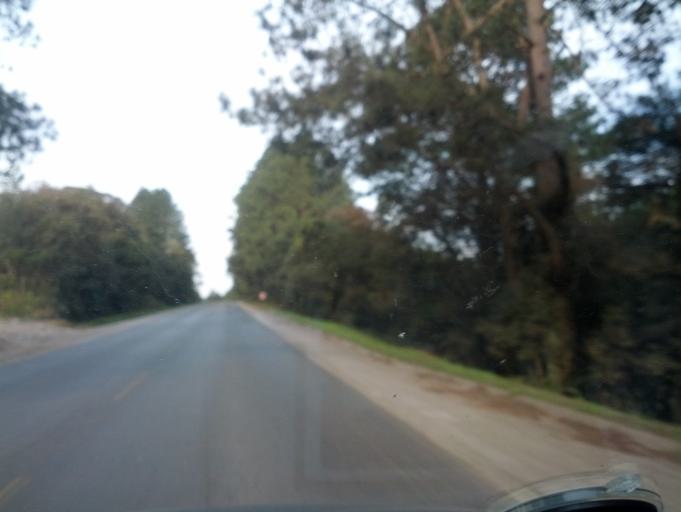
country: BR
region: Santa Catarina
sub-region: Otacilio Costa
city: Otacilio Costa
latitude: -27.3096
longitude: -50.1285
